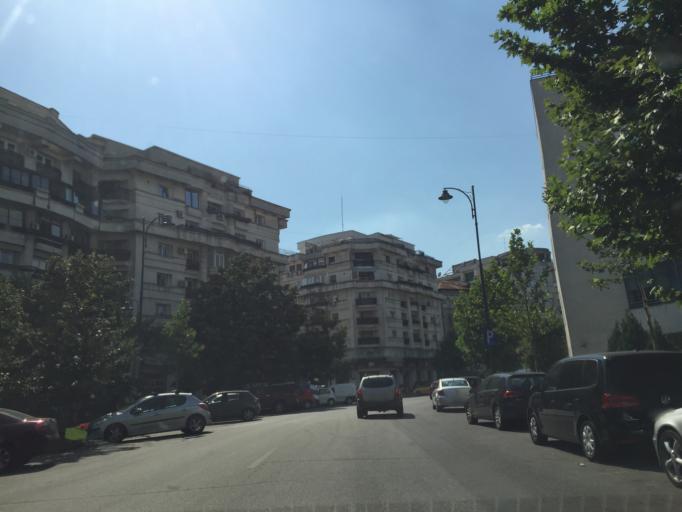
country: RO
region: Bucuresti
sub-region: Municipiul Bucuresti
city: Bucharest
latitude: 44.4282
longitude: 26.1097
